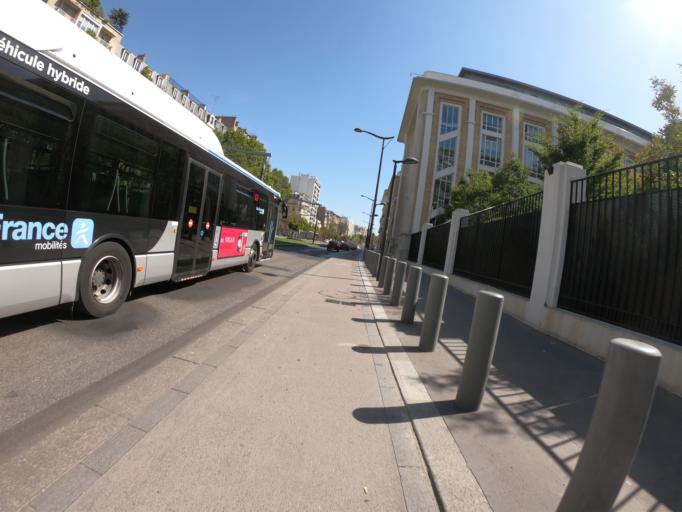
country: FR
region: Ile-de-France
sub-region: Departement des Hauts-de-Seine
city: Vanves
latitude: 48.8349
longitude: 2.2823
